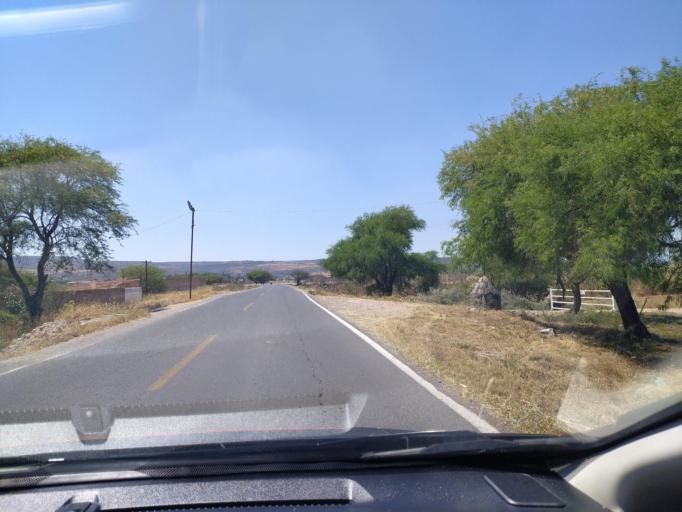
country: MX
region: Guanajuato
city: Ciudad Manuel Doblado
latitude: 20.7412
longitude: -101.9381
